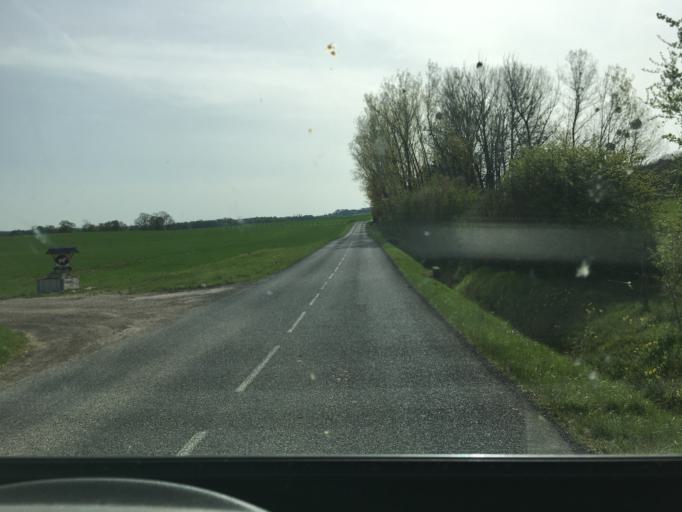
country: FR
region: Lorraine
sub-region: Departement de Meurthe-et-Moselle
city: Dommartin-les-Toul
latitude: 48.6690
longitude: 5.9402
